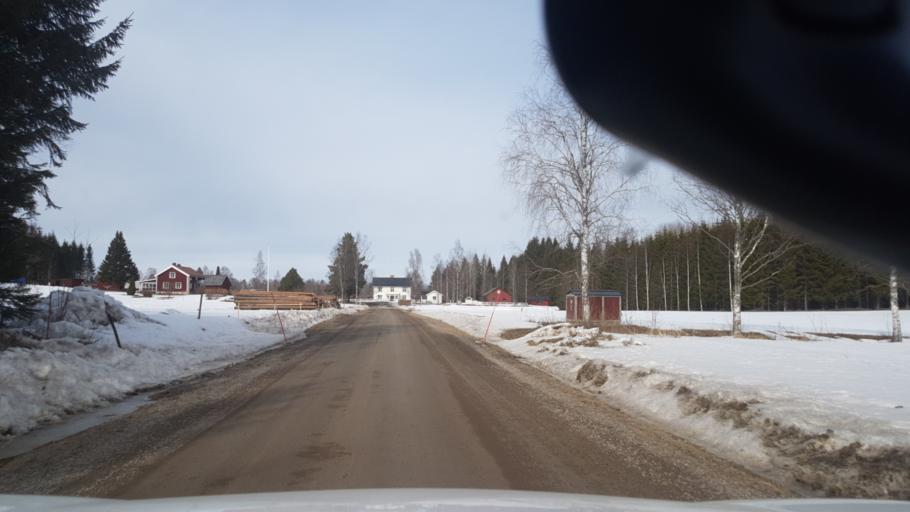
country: SE
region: Vaermland
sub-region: Eda Kommun
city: Charlottenberg
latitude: 59.8405
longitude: 12.3587
